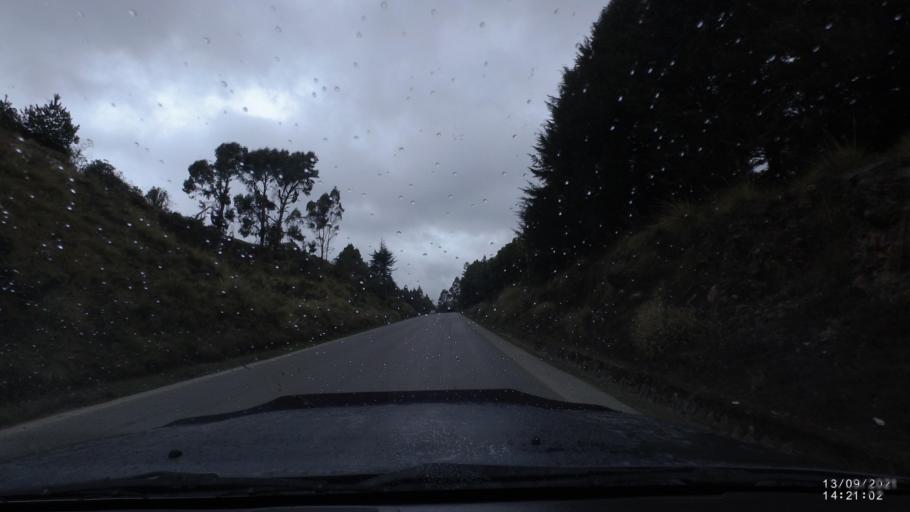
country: BO
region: Cochabamba
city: Colomi
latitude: -17.2561
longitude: -65.8914
